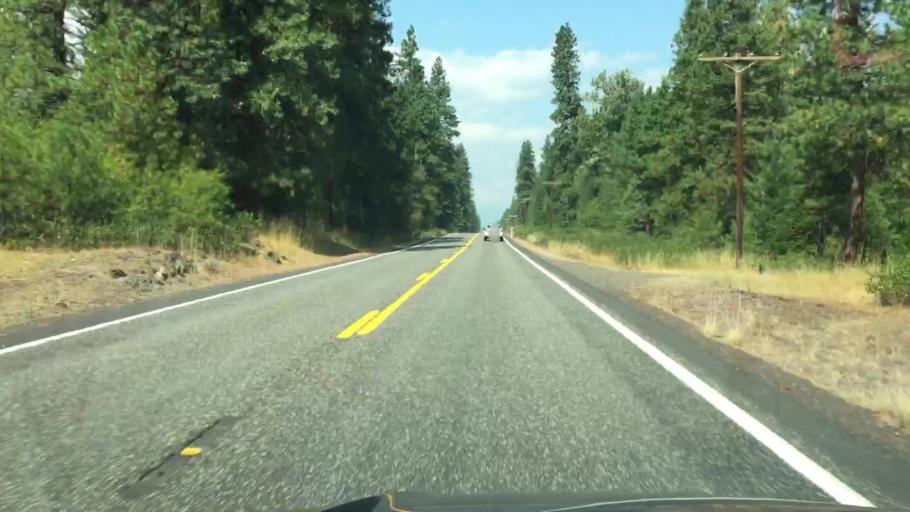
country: US
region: Washington
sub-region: Klickitat County
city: White Salmon
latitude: 45.9776
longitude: -121.5041
